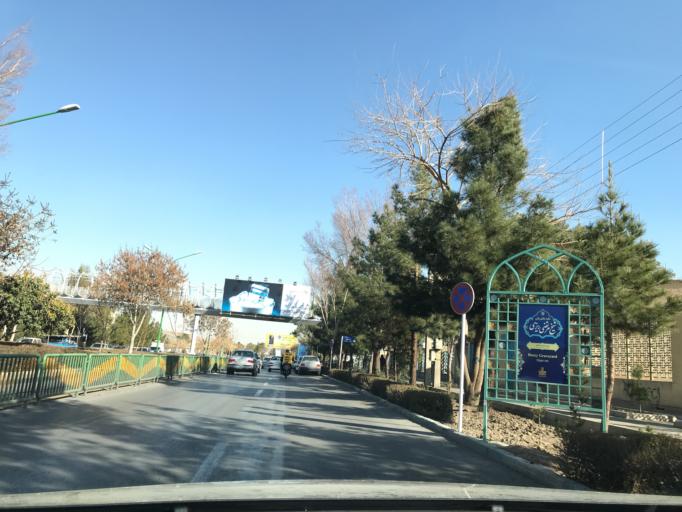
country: IR
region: Isfahan
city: Isfahan
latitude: 32.6219
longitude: 51.6766
